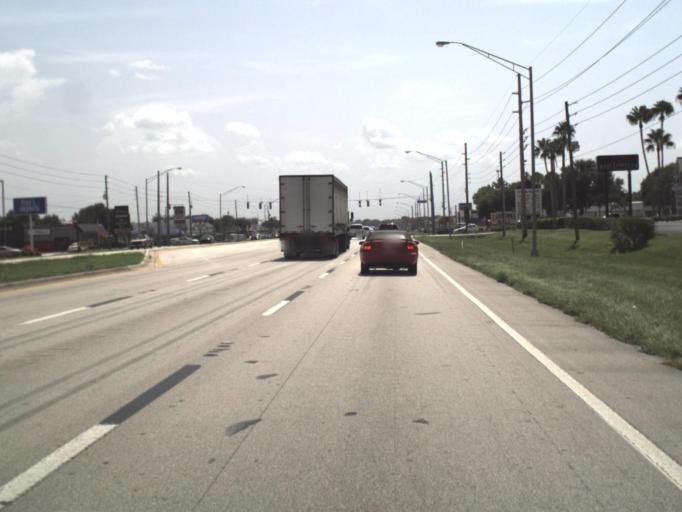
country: US
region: Florida
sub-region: Highlands County
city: Sebring
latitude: 27.4911
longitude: -81.4842
